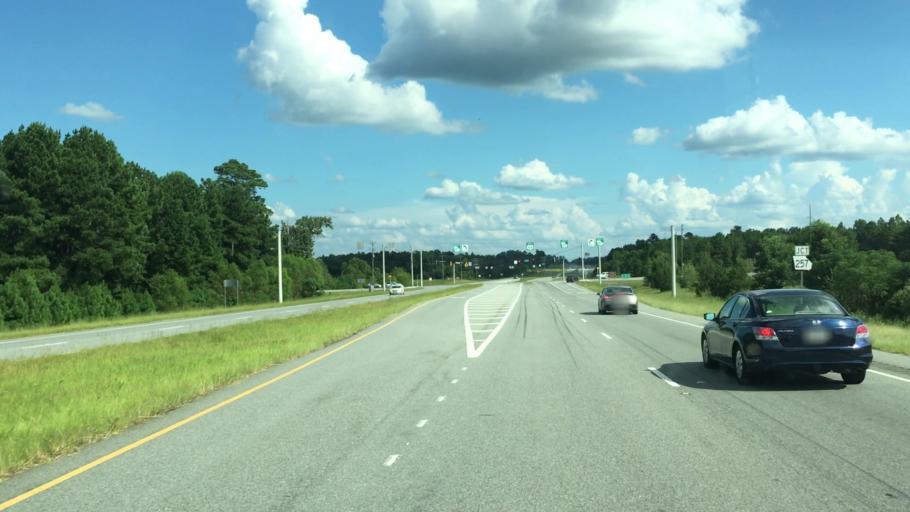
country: US
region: Georgia
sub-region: Laurens County
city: Dublin
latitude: 32.5173
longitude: -82.9582
